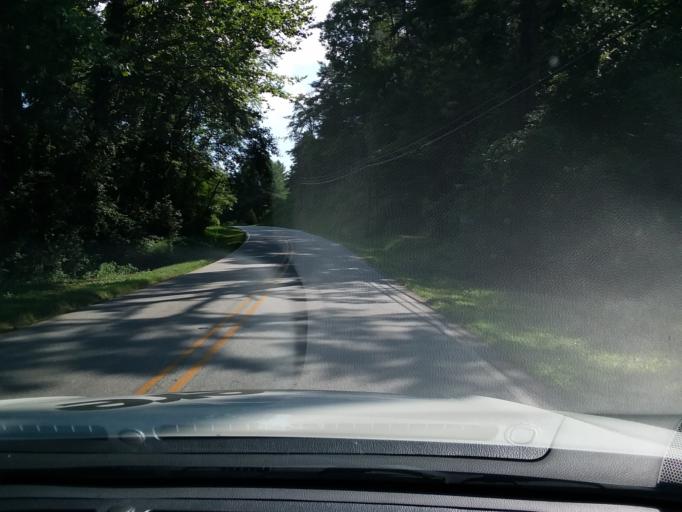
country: US
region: Georgia
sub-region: Rabun County
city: Clayton
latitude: 34.8451
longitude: -83.4351
